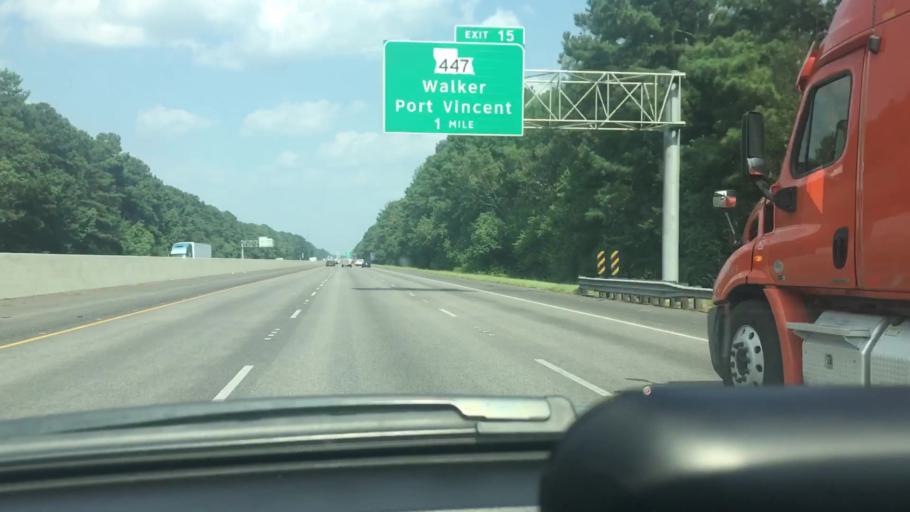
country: US
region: Louisiana
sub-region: Livingston Parish
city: Walker
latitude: 30.4672
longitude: -90.8840
